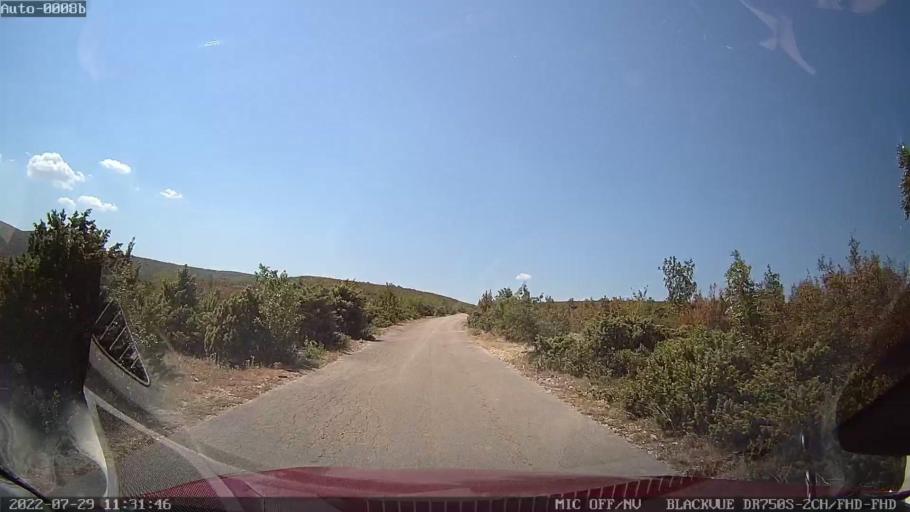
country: HR
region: Zadarska
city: Obrovac
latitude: 44.1948
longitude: 15.7448
